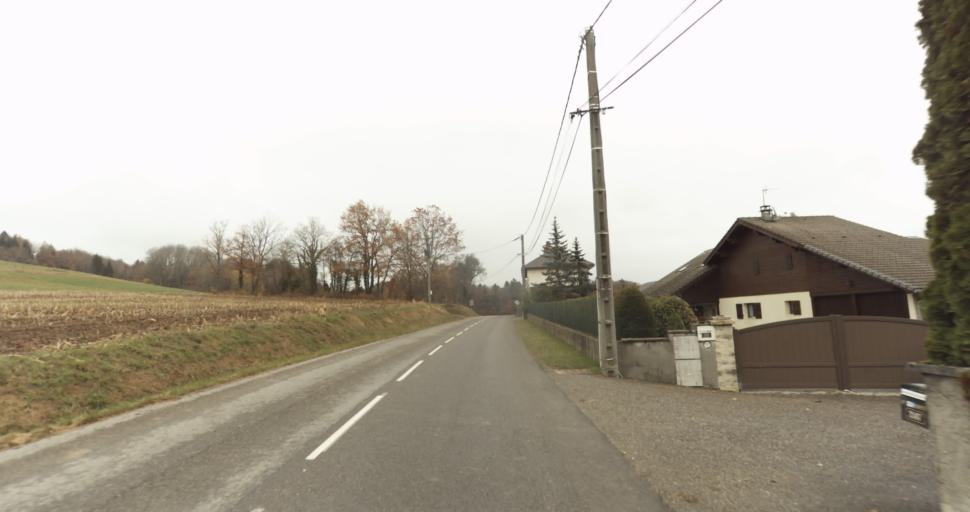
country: FR
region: Rhone-Alpes
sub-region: Departement de la Haute-Savoie
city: Evires
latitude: 46.0386
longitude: 6.2136
